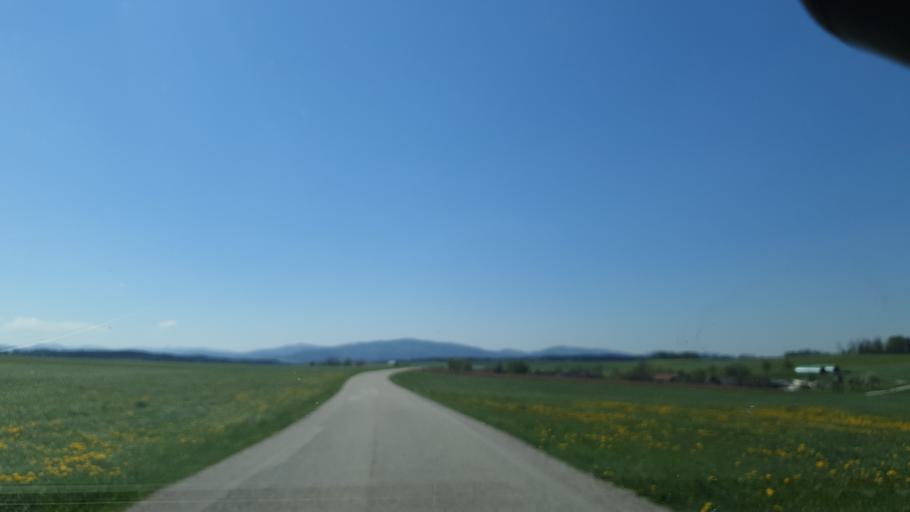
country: AT
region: Upper Austria
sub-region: Politischer Bezirk Vocklabruck
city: Gampern
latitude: 47.9767
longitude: 13.5414
